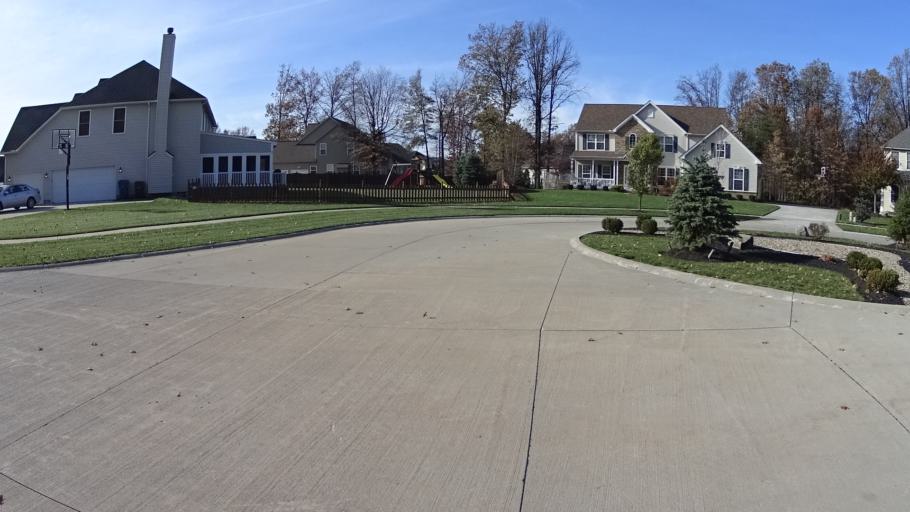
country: US
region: Ohio
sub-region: Lorain County
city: Avon Lake
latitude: 41.5001
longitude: -81.9850
